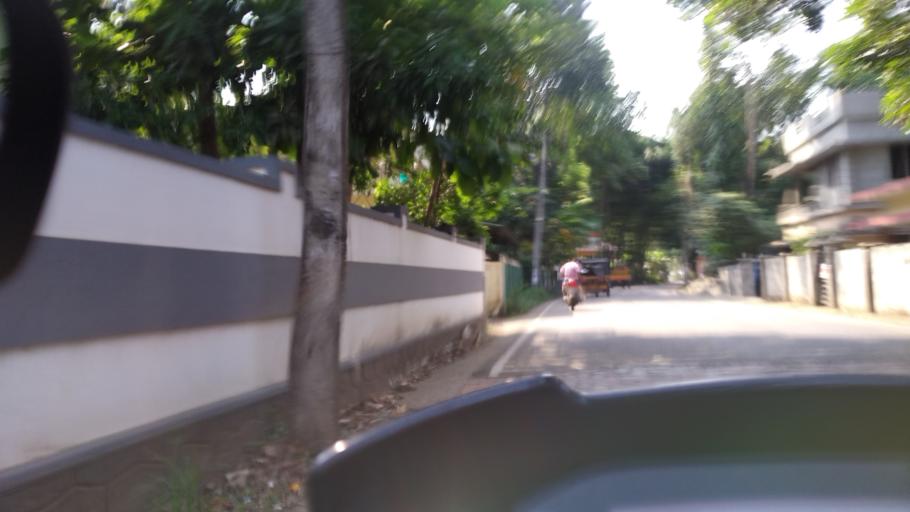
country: IN
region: Kerala
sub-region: Ernakulam
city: Piravam
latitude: 9.8682
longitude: 76.5039
